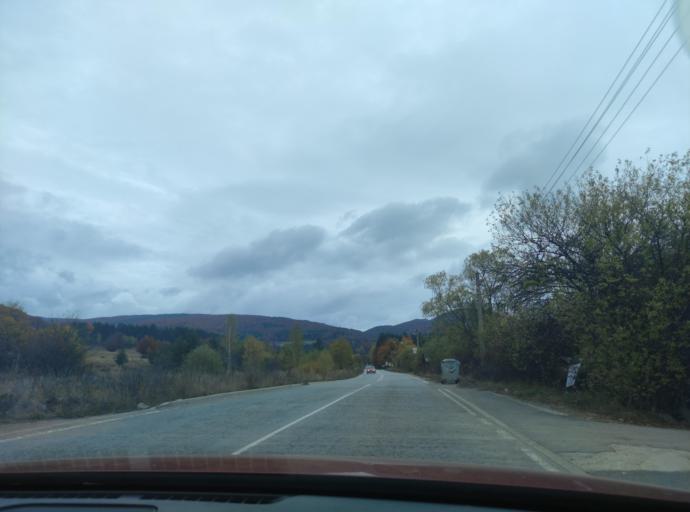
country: BG
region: Sofiya
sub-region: Obshtina Godech
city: Godech
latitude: 43.0968
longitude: 23.1003
